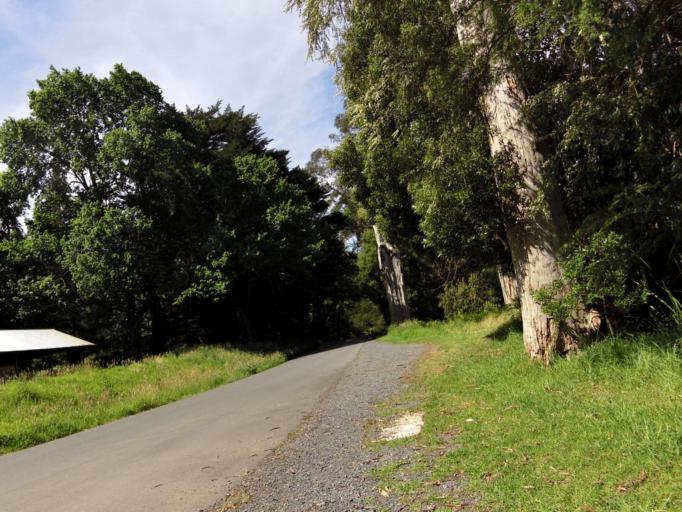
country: AU
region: Victoria
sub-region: Yarra Ranges
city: Millgrove
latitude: -37.7549
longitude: 145.6791
